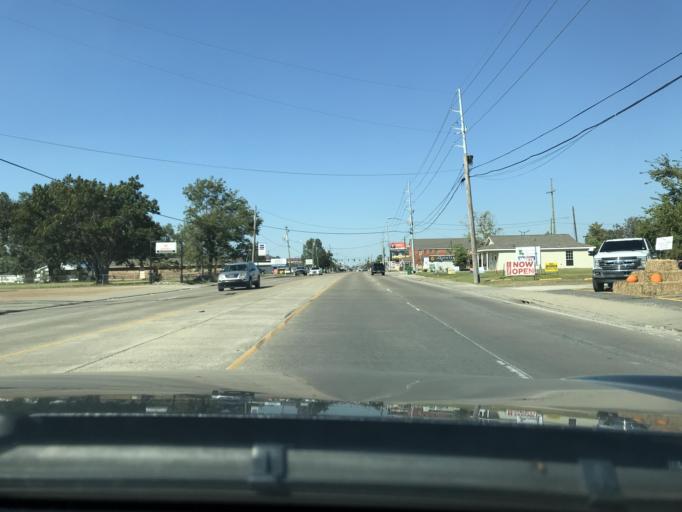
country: US
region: Louisiana
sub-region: Calcasieu Parish
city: Westlake
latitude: 30.2450
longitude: -93.2581
